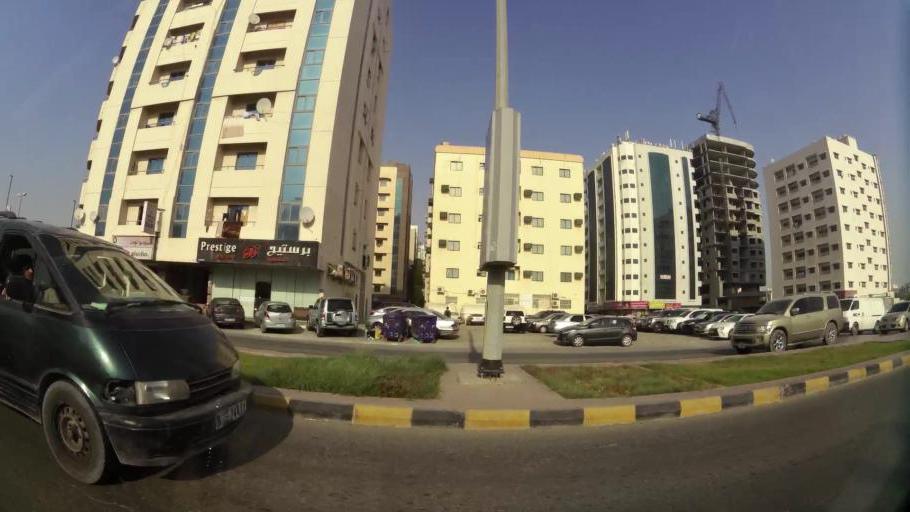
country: AE
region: Ajman
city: Ajman
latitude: 25.3887
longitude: 55.4457
